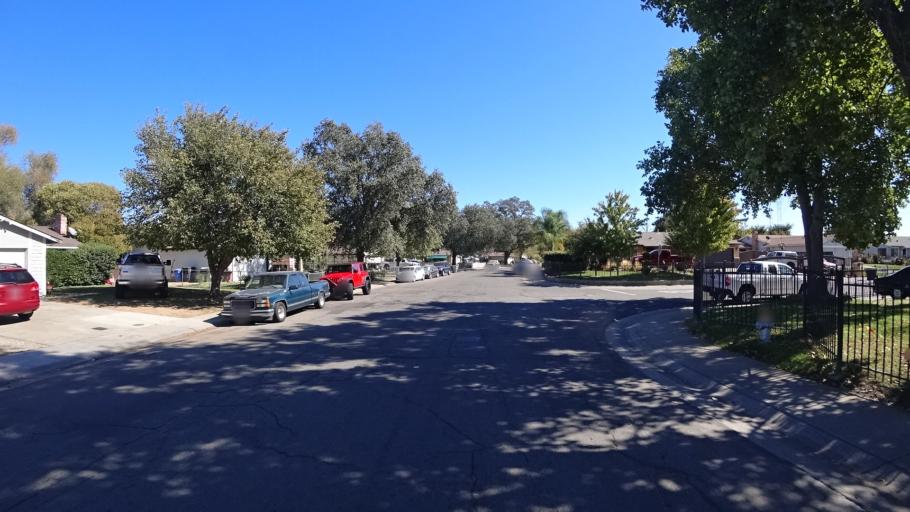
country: US
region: California
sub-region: Sacramento County
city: Parkway
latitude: 38.4714
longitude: -121.4400
